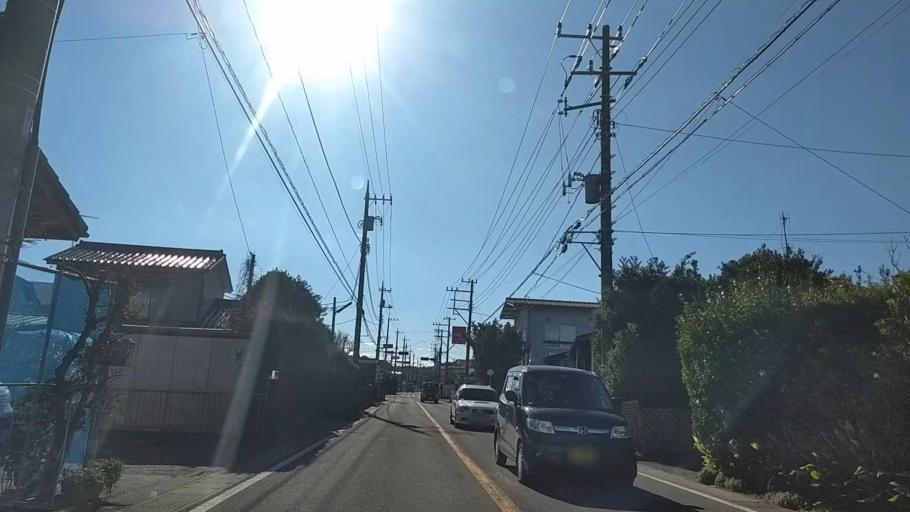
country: JP
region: Chiba
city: Tateyama
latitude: 34.9810
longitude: 139.8630
